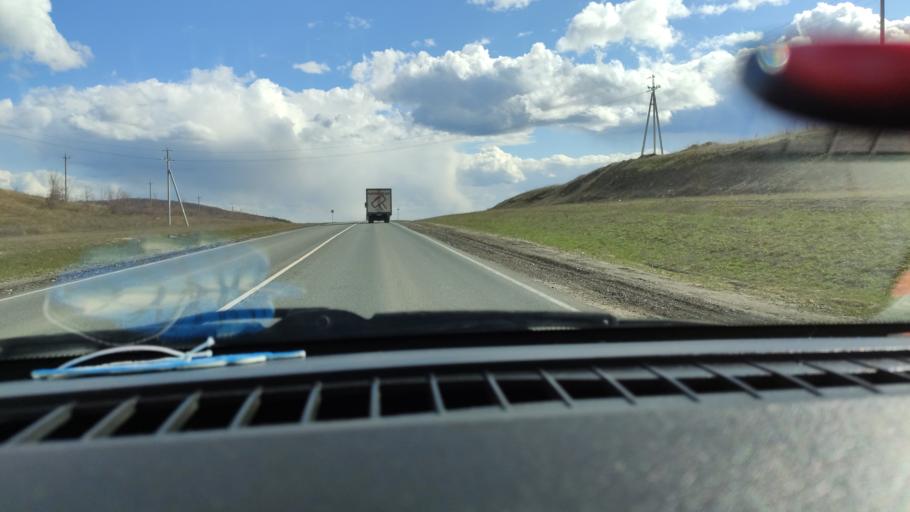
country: RU
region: Saratov
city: Alekseyevka
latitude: 52.3188
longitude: 47.9222
